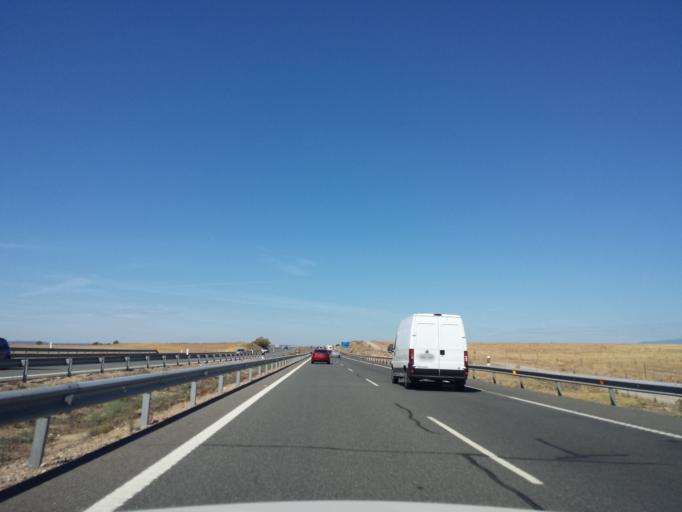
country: ES
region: Extremadura
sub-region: Provincia de Caceres
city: Berrocalejo
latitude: 39.8948
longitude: -5.3560
